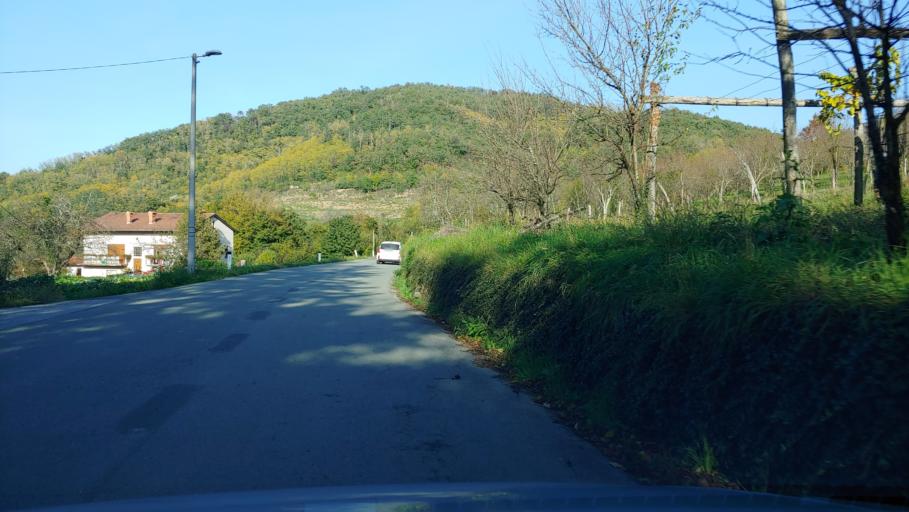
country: SI
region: Ajdovscina
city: Ajdovscina
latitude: 45.8129
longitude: 13.8864
